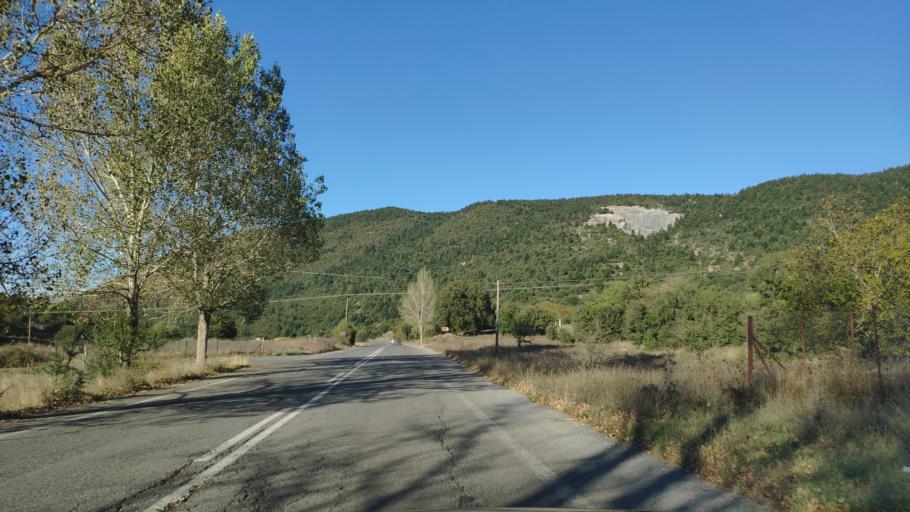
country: GR
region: Peloponnese
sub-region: Nomos Arkadias
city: Langadhia
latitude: 37.6928
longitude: 22.1969
